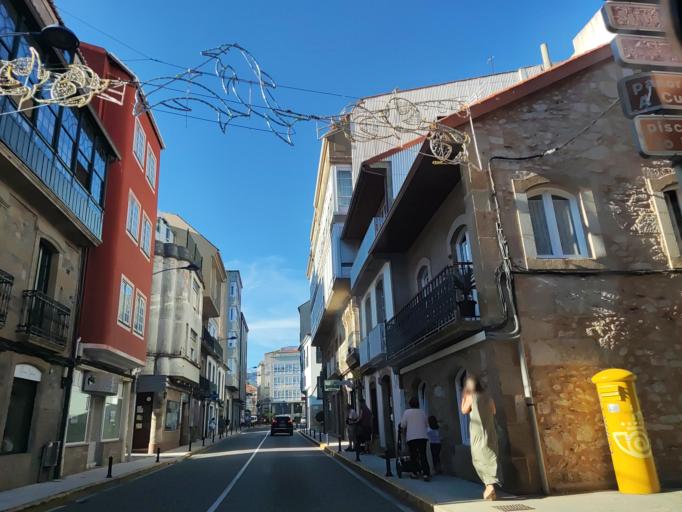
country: ES
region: Galicia
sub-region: Provincia da Coruna
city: Boiro
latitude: 42.6034
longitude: -8.9389
